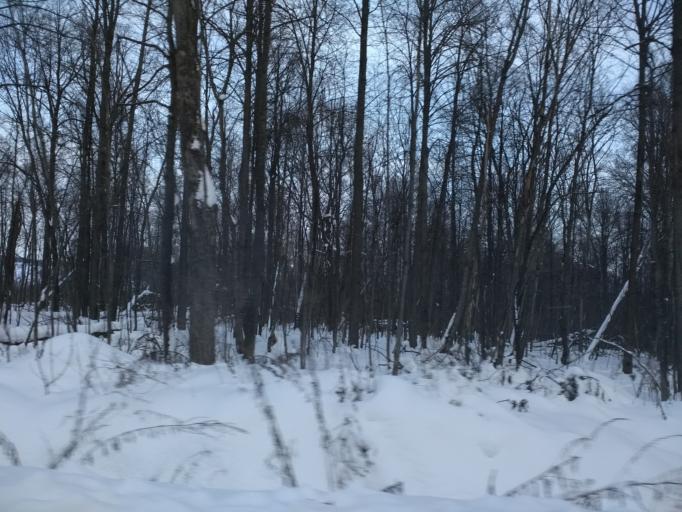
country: RU
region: Bashkortostan
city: Kudeyevskiy
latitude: 54.7151
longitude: 56.6339
